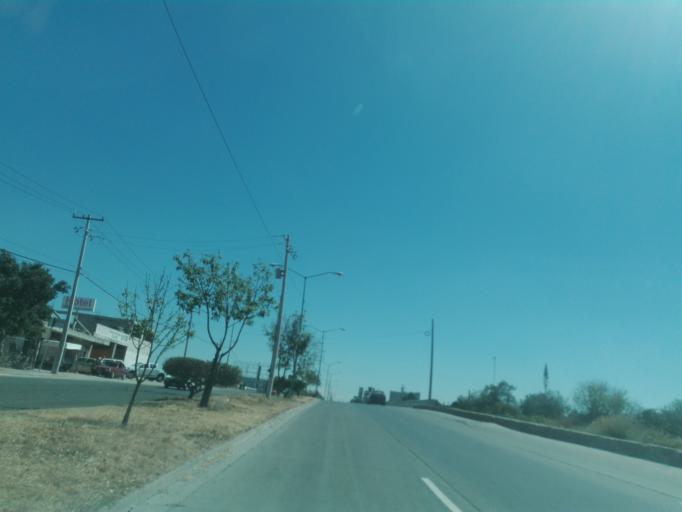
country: MX
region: Guanajuato
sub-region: Leon
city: San Jose de Duran (Los Troncoso)
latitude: 21.0897
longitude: -101.6756
